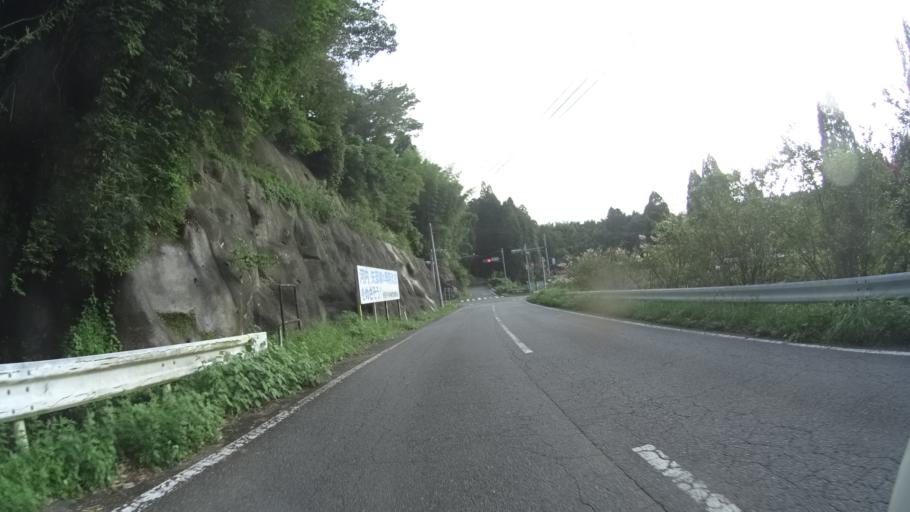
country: JP
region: Kumamoto
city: Ozu
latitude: 32.6868
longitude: 131.0112
